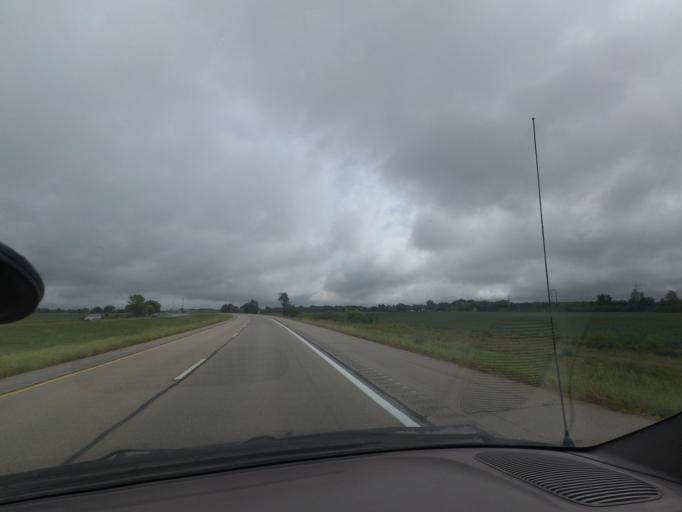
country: US
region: Illinois
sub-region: Piatt County
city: Monticello
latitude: 40.0316
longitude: -88.6049
